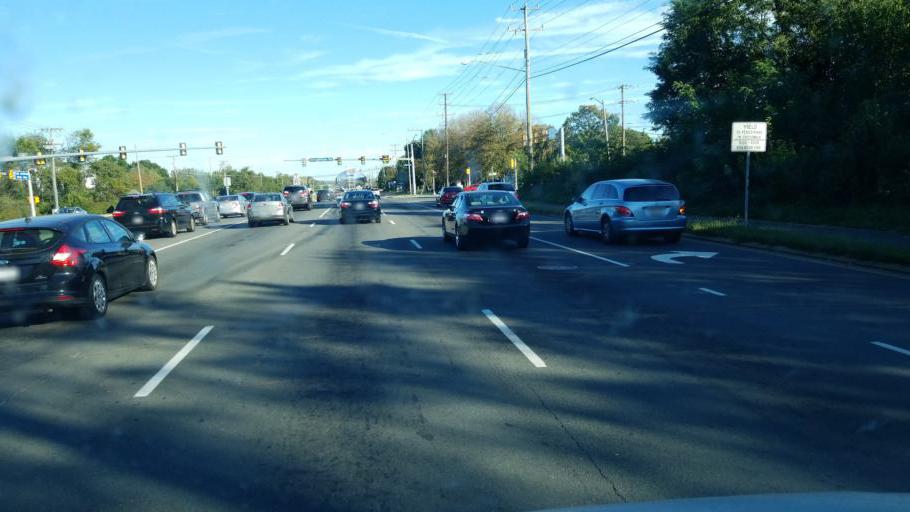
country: US
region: Virginia
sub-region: Fairfax County
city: Greenbriar
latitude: 38.8845
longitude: -77.4067
